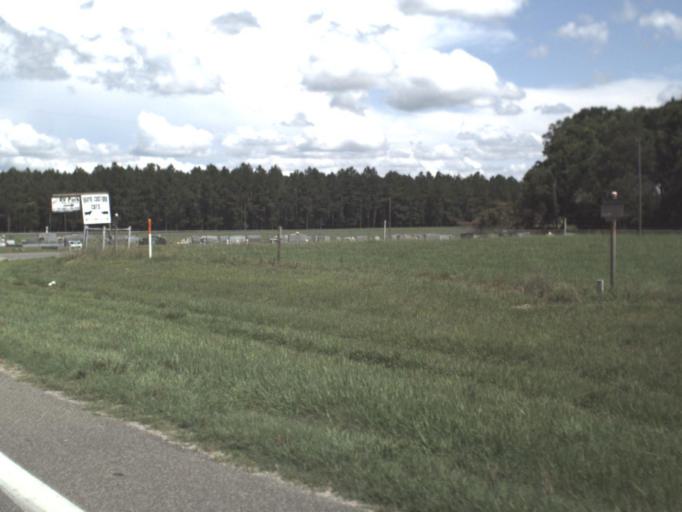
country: US
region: Florida
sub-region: Lafayette County
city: Mayo
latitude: 30.0533
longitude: -83.1135
